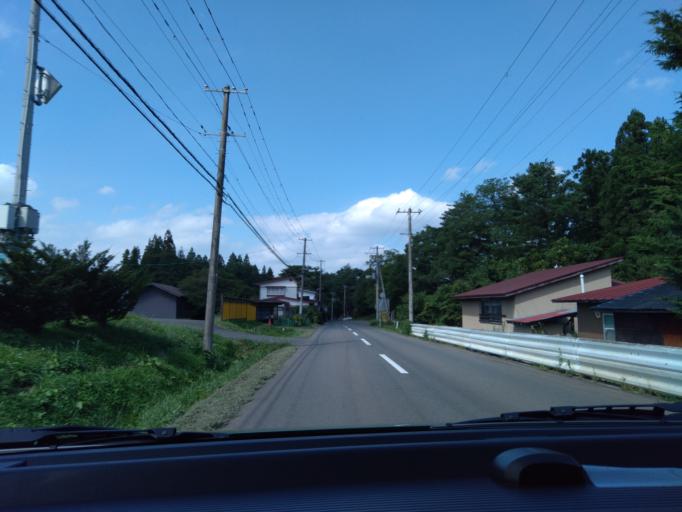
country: JP
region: Iwate
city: Shizukuishi
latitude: 39.6515
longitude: 140.9928
